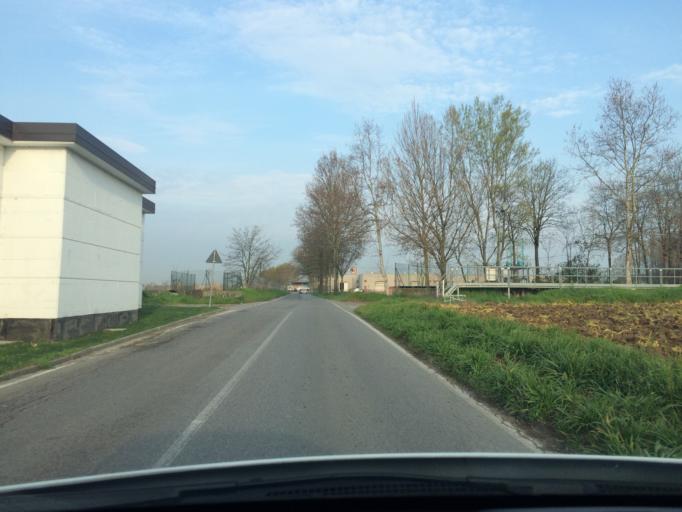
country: IT
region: Lombardy
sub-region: Provincia di Brescia
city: Flero
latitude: 45.4877
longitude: 10.1681
